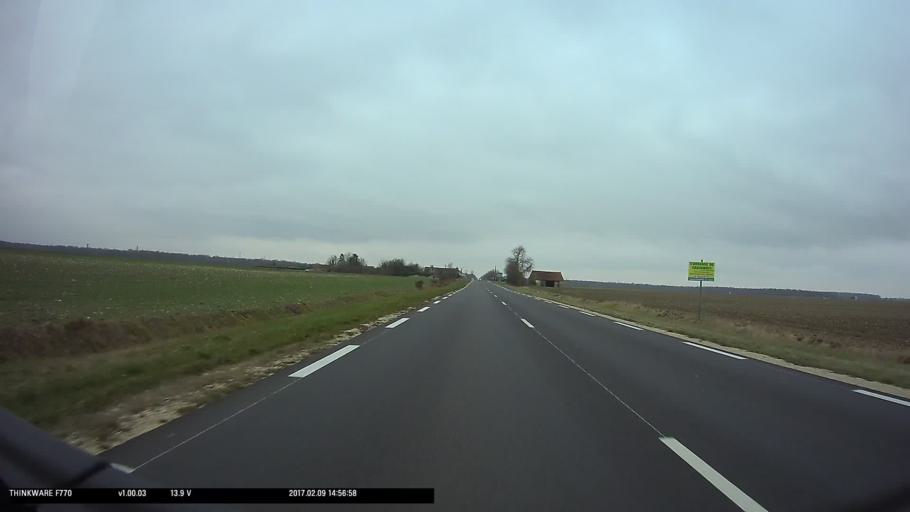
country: FR
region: Centre
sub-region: Departement du Cher
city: Levet
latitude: 46.8589
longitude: 2.4196
